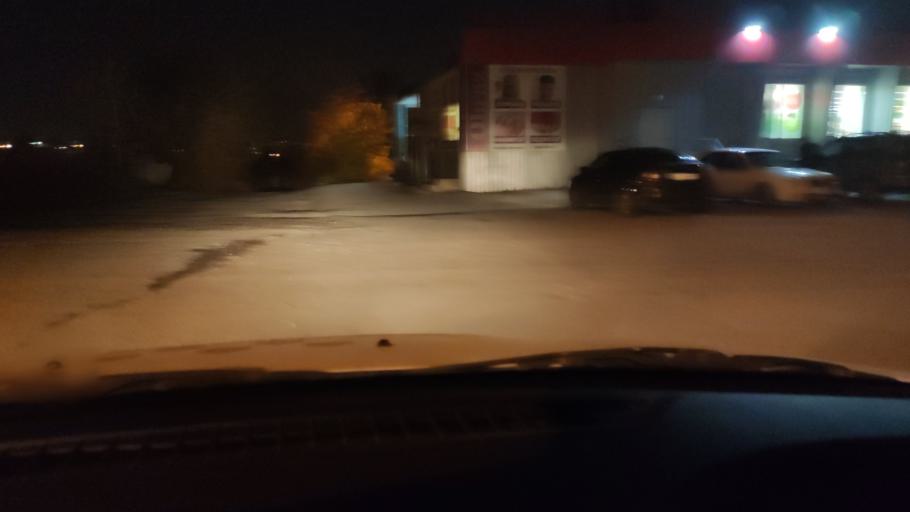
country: RU
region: Perm
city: Perm
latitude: 57.9781
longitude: 56.2981
